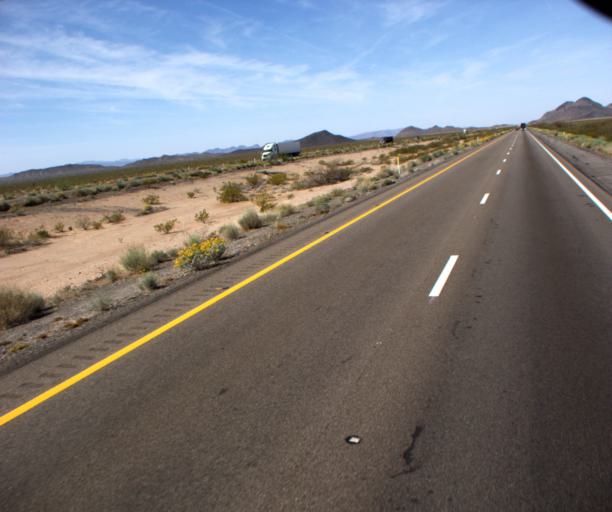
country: US
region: Arizona
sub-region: La Paz County
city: Salome
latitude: 33.6019
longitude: -113.5700
